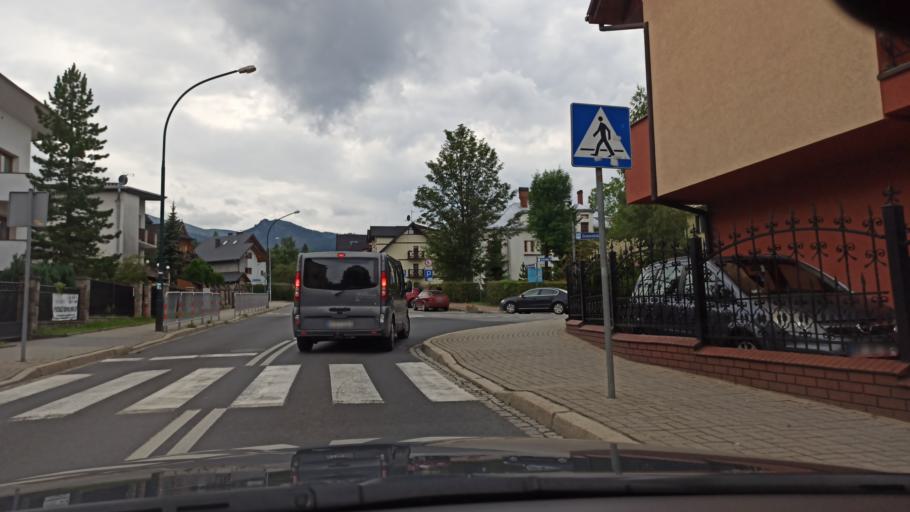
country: PL
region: Lesser Poland Voivodeship
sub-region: Powiat tatrzanski
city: Zakopane
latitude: 49.2866
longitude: 19.9568
